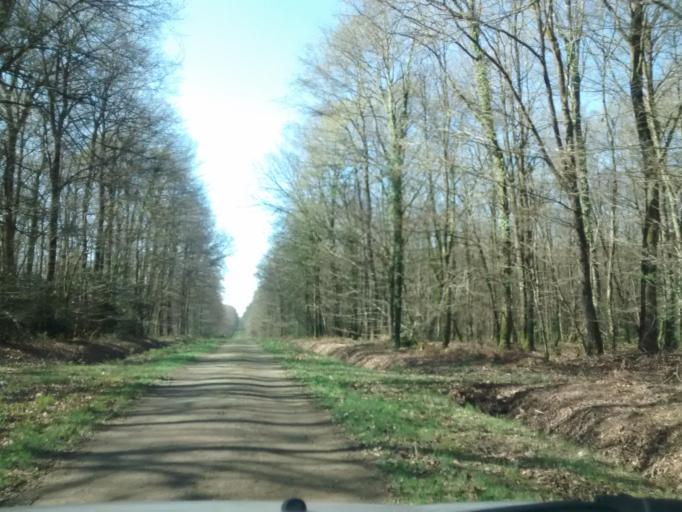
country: FR
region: Brittany
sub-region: Departement d'Ille-et-Vilaine
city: Chasne-sur-Illet
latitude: 48.2240
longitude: -1.5458
